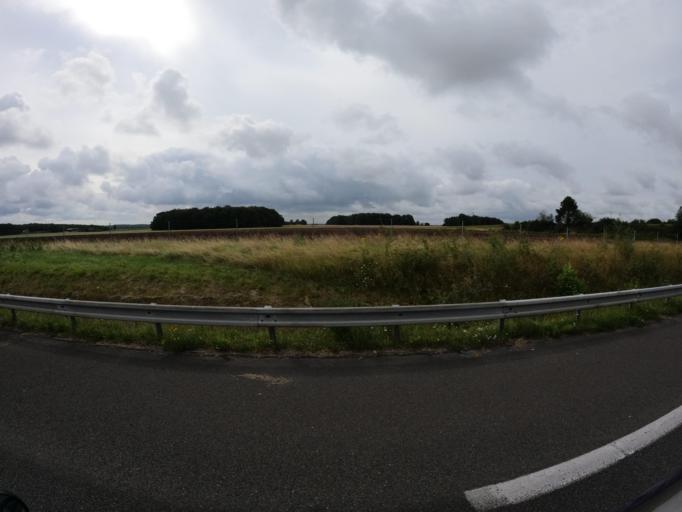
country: FR
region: Centre
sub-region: Departement du Loir-et-Cher
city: Herbault
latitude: 47.5858
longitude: 1.0782
